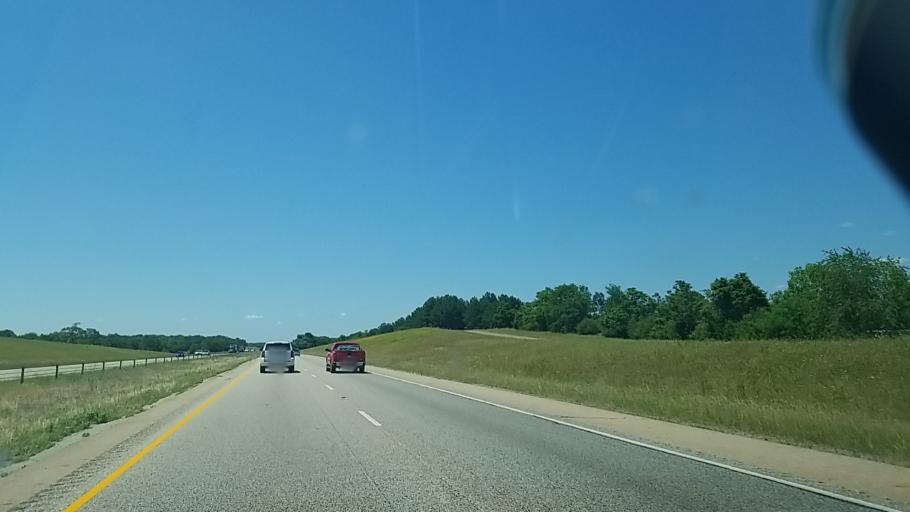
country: US
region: Texas
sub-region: Leon County
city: Buffalo
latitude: 31.3908
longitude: -96.0287
